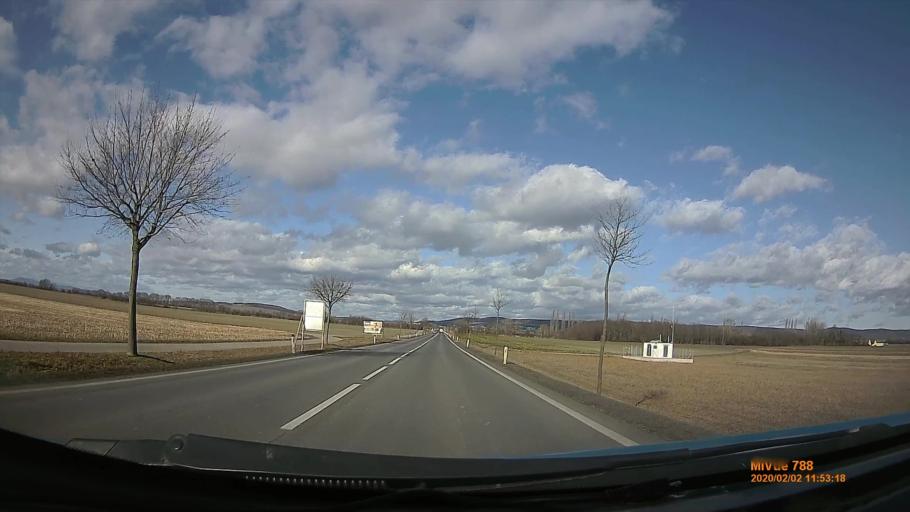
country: AT
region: Burgenland
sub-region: Eisenstadt-Umgebung
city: Zagersdorf
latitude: 47.7827
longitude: 16.5199
